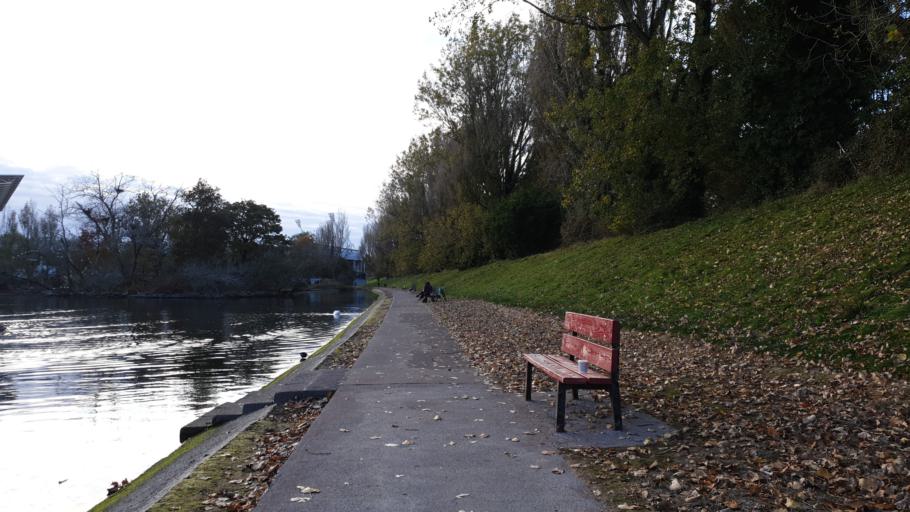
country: IE
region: Munster
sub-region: County Cork
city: Cork
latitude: 51.9001
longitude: -8.4300
